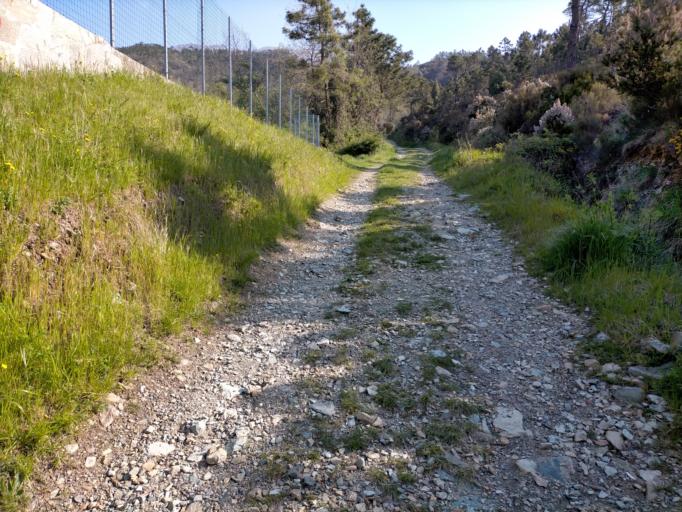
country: IT
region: Liguria
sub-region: Provincia di Genova
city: Sciarborasca
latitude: 44.4054
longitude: 8.6091
